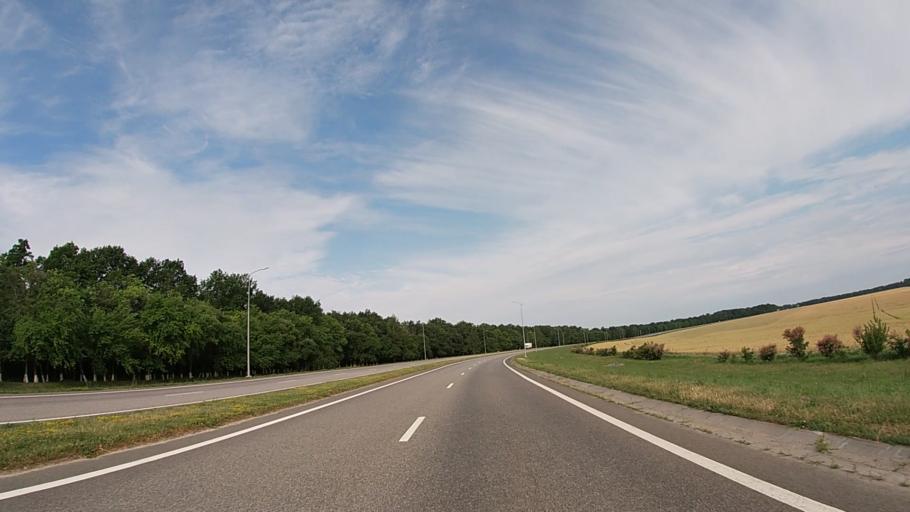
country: RU
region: Belgorod
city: Borisovka
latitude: 50.7515
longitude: 35.9745
